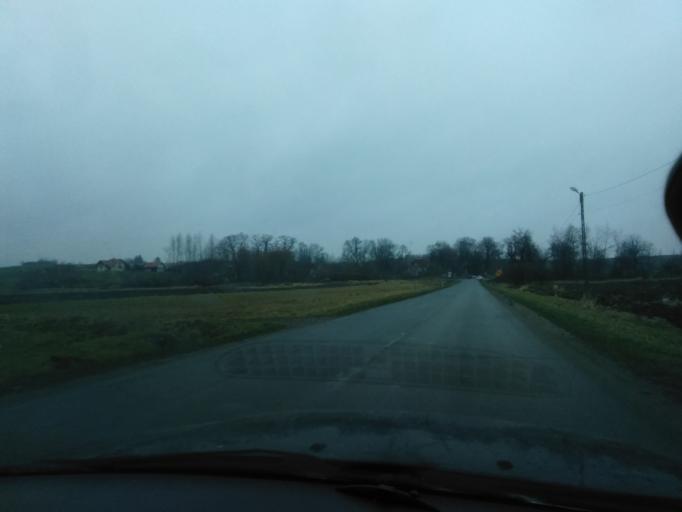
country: PL
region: Subcarpathian Voivodeship
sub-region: Powiat jaroslawski
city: Pruchnik
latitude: 49.9052
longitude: 22.5468
